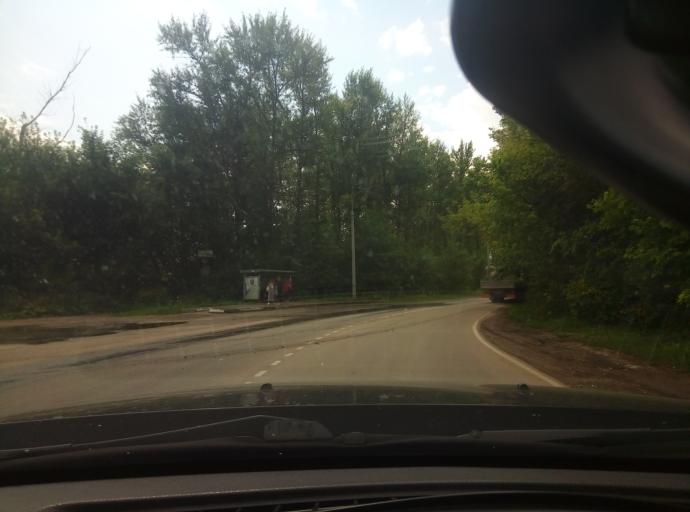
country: RU
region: Tula
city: Borodinskiy
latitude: 53.9939
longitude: 37.8113
